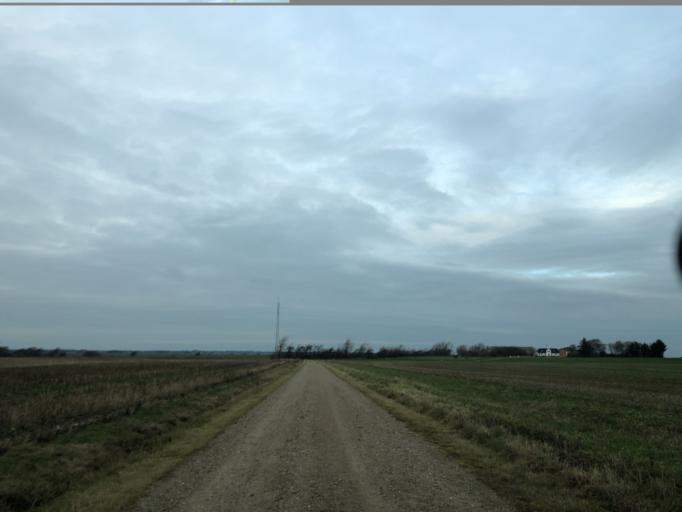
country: DK
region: Central Jutland
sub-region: Holstebro Kommune
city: Ulfborg
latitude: 56.2736
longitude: 8.2170
